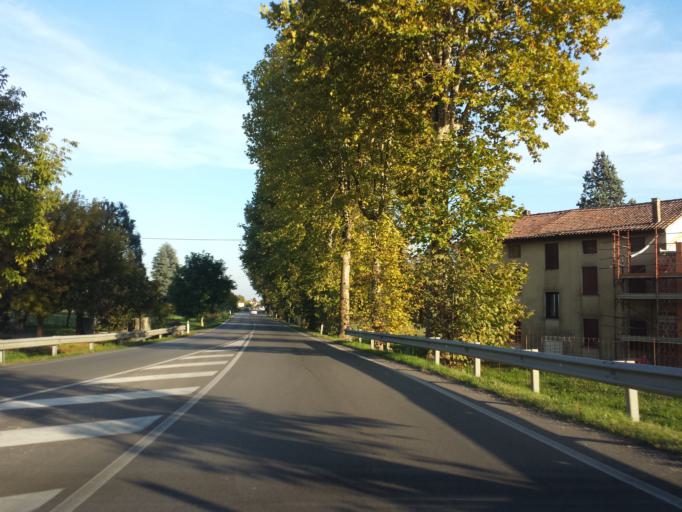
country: IT
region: Veneto
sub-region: Provincia di Vicenza
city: Castelnovo
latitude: 45.6096
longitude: 11.4722
